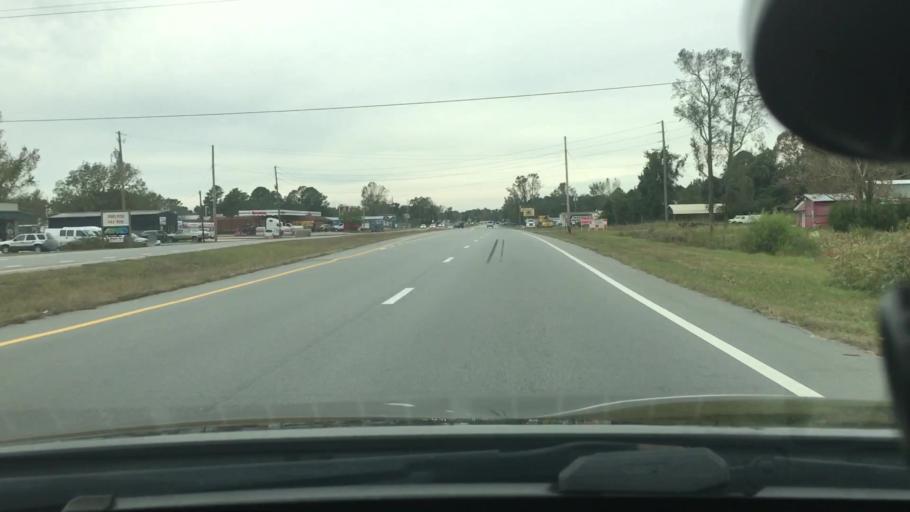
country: US
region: North Carolina
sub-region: Craven County
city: New Bern
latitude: 35.1206
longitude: -77.0177
